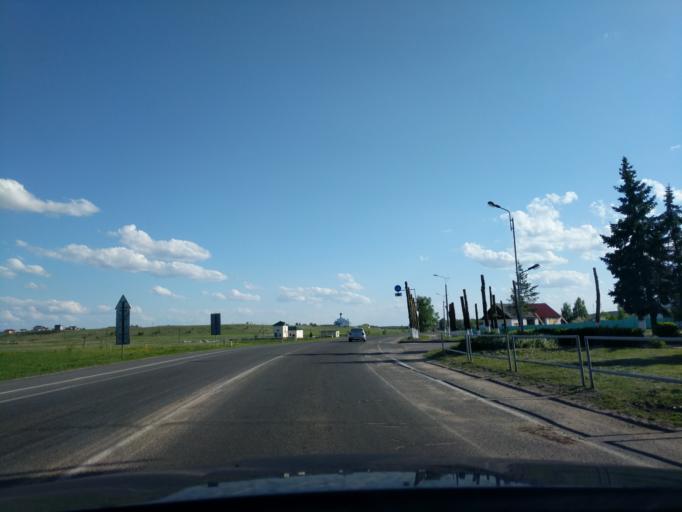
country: BY
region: Minsk
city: Myadzyel
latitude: 54.8758
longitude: 26.9413
